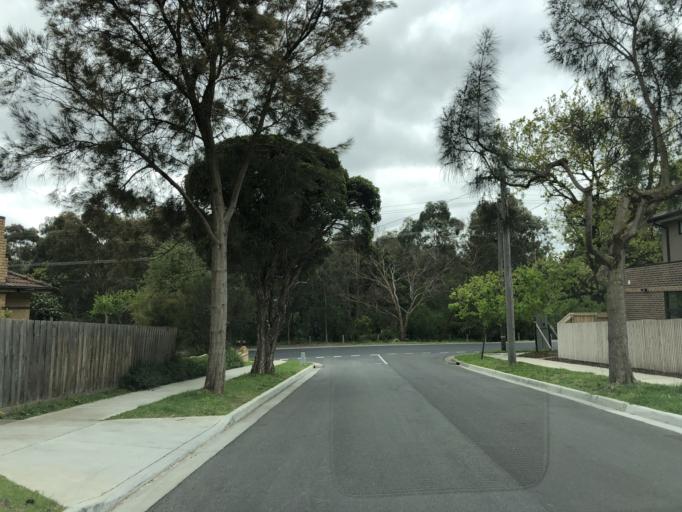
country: AU
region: Victoria
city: Burwood East
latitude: -37.8428
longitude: 145.1412
